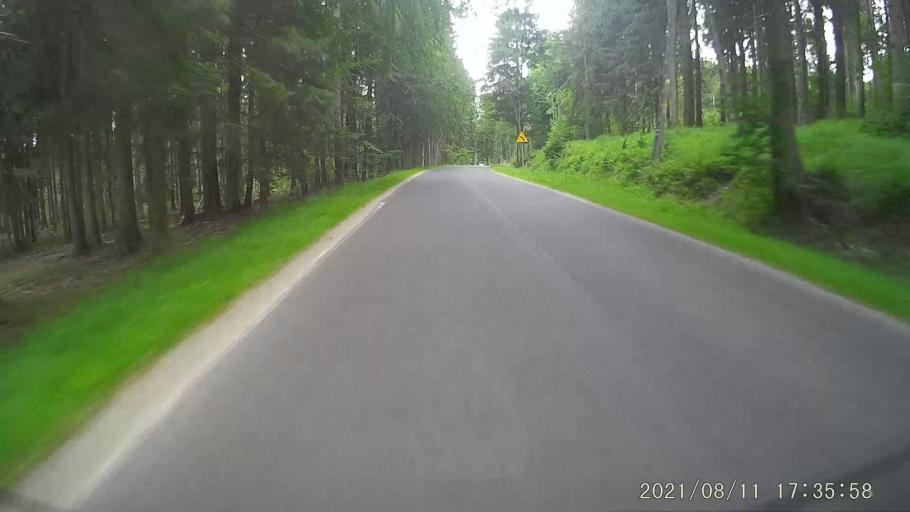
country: PL
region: Lower Silesian Voivodeship
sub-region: Powiat klodzki
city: Duszniki-Zdroj
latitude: 50.3260
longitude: 16.4104
